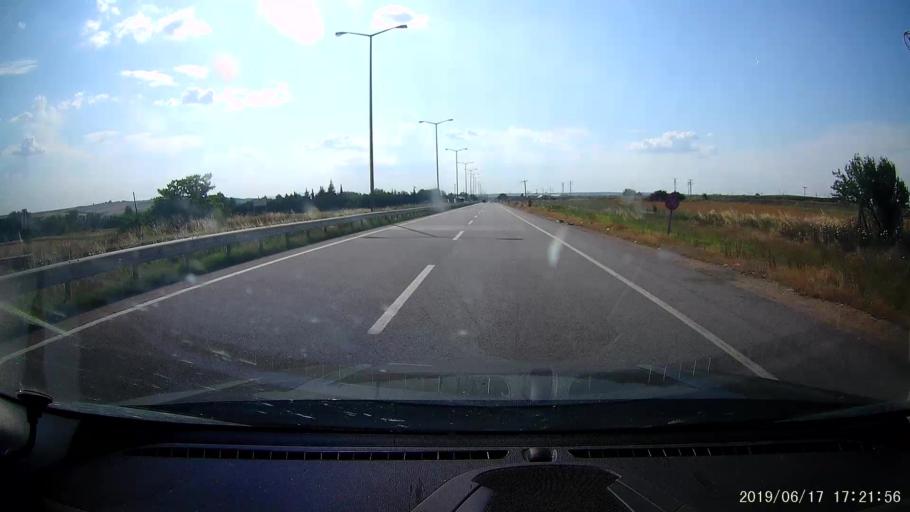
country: GR
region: East Macedonia and Thrace
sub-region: Nomos Evrou
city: Rizia
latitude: 41.7088
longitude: 26.3848
